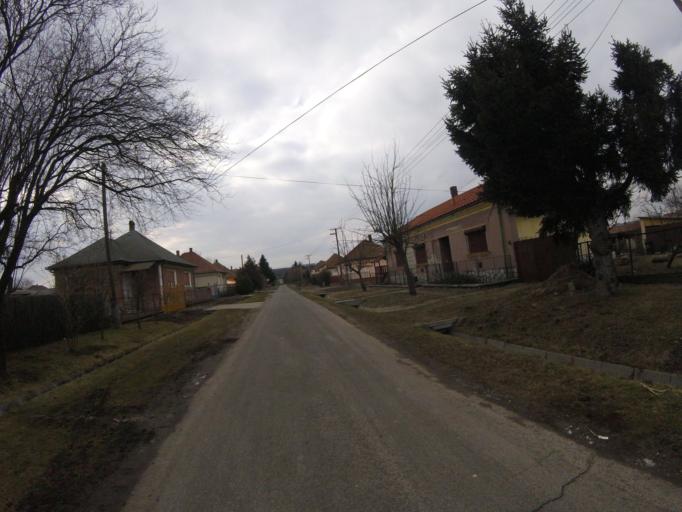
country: HU
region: Heves
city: Egerszalok
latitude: 47.8676
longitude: 20.3246
